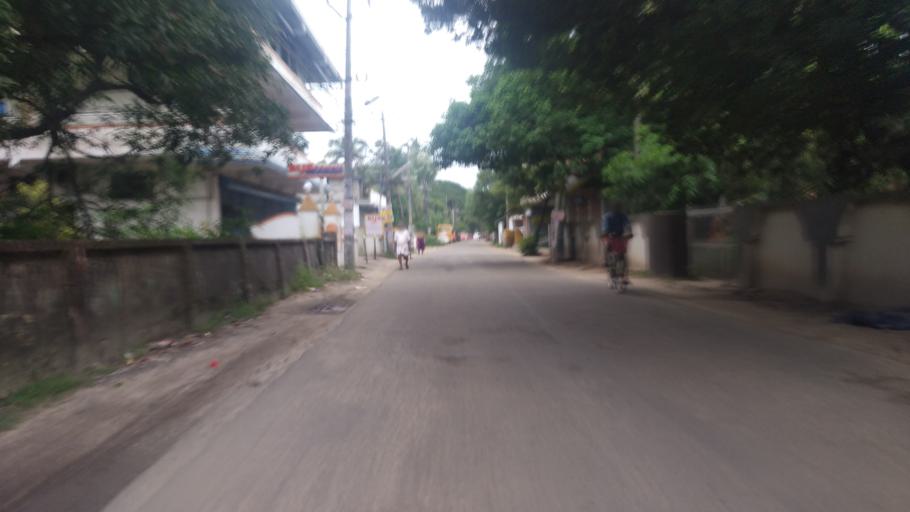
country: IN
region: Kerala
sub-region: Alappuzha
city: Arukutti
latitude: 9.8712
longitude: 76.2904
